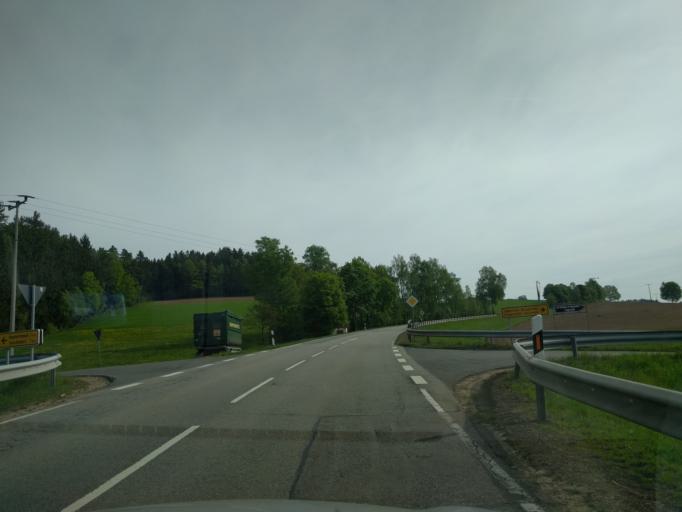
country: DE
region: Bavaria
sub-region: Upper Palatinate
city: Michelsneukirchen
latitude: 49.1156
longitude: 12.5204
